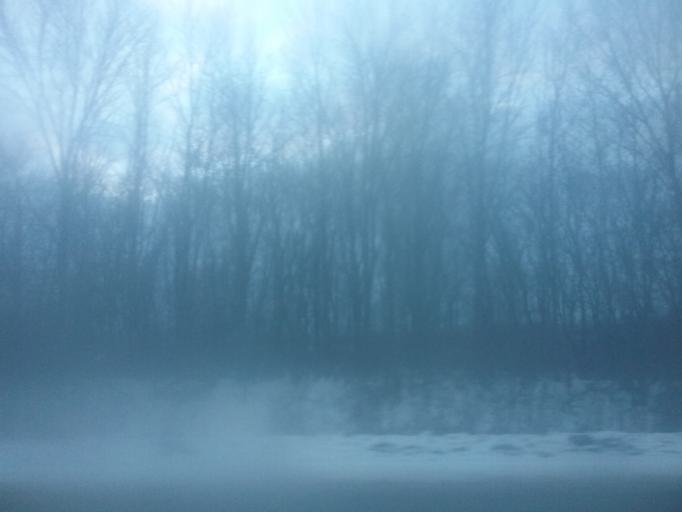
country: RU
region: Tula
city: Bolokhovo
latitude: 54.0459
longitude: 37.8529
